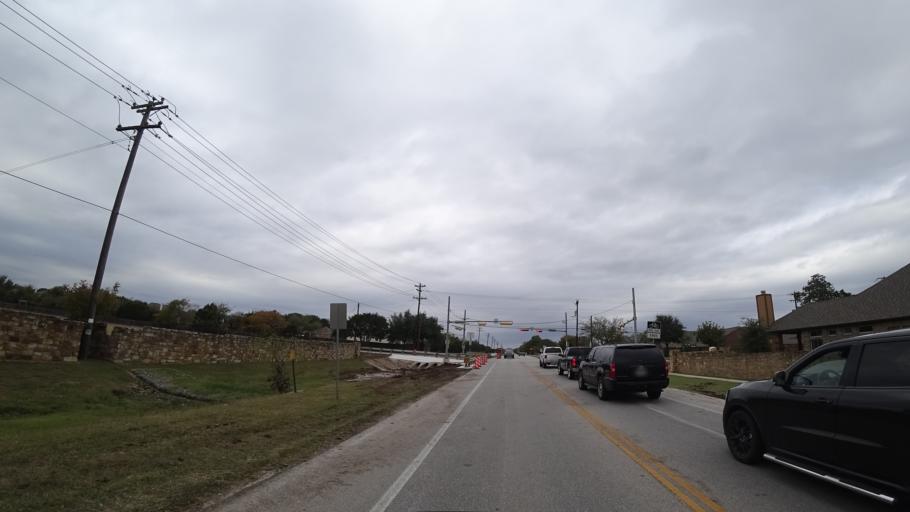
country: US
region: Texas
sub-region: Travis County
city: Shady Hollow
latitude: 30.1479
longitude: -97.8546
